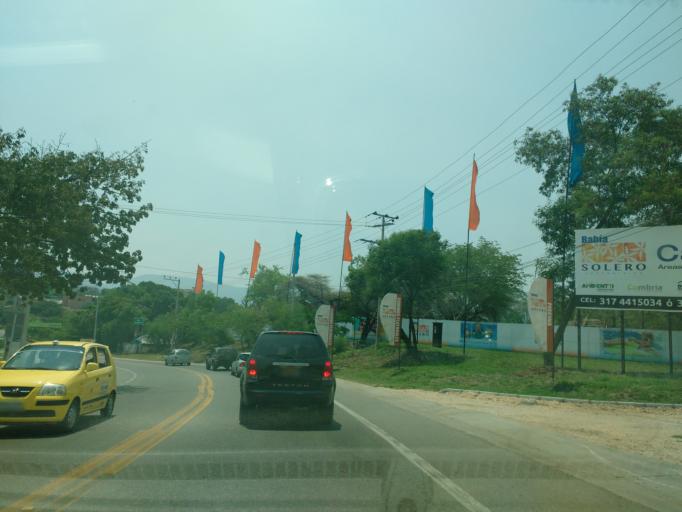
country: CO
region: Cundinamarca
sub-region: Girardot
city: Girardot City
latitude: 4.3011
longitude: -74.7934
